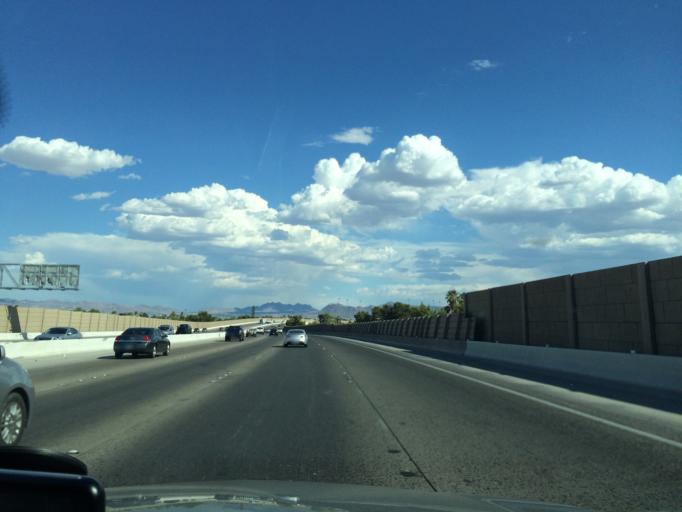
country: US
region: Nevada
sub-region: Clark County
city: Winchester
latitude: 36.1279
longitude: -115.0881
